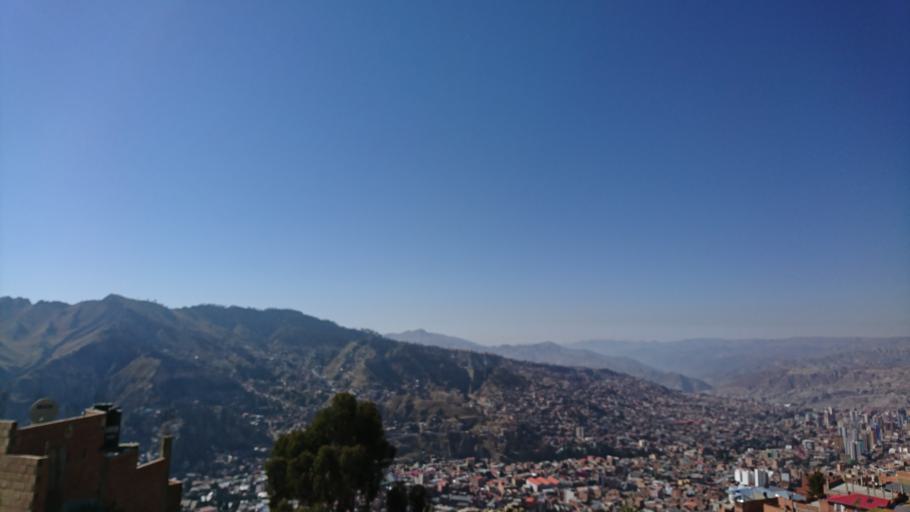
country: BO
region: La Paz
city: La Paz
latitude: -16.4700
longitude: -68.1249
